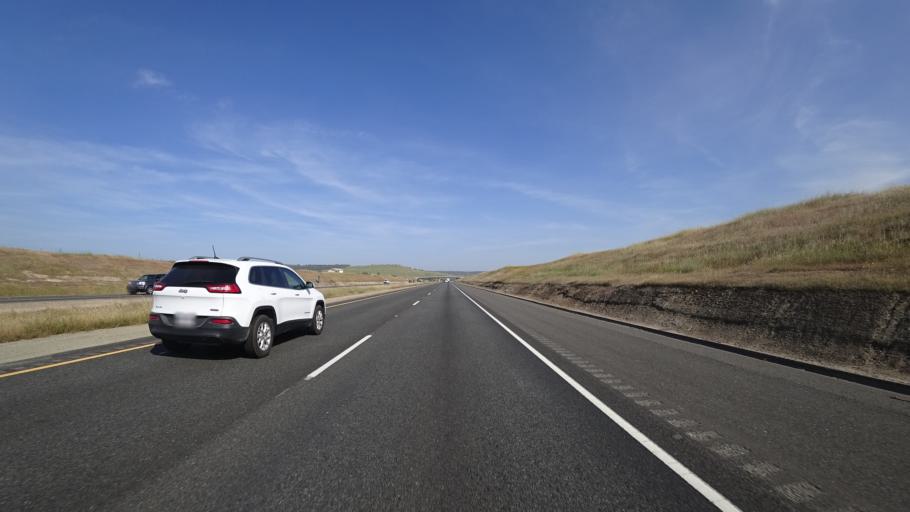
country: US
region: California
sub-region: Butte County
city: Thermalito
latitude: 39.5910
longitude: -121.6401
